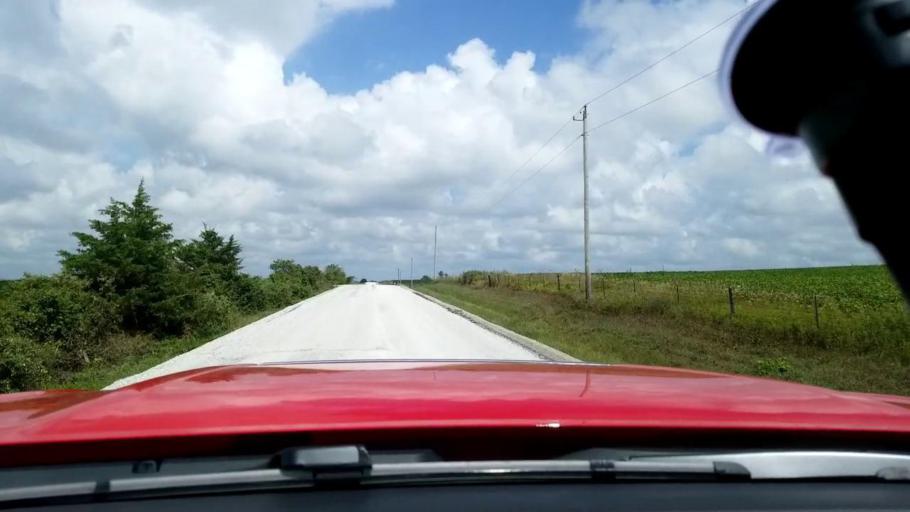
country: US
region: Iowa
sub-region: Decatur County
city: Lamoni
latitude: 40.6648
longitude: -94.0483
